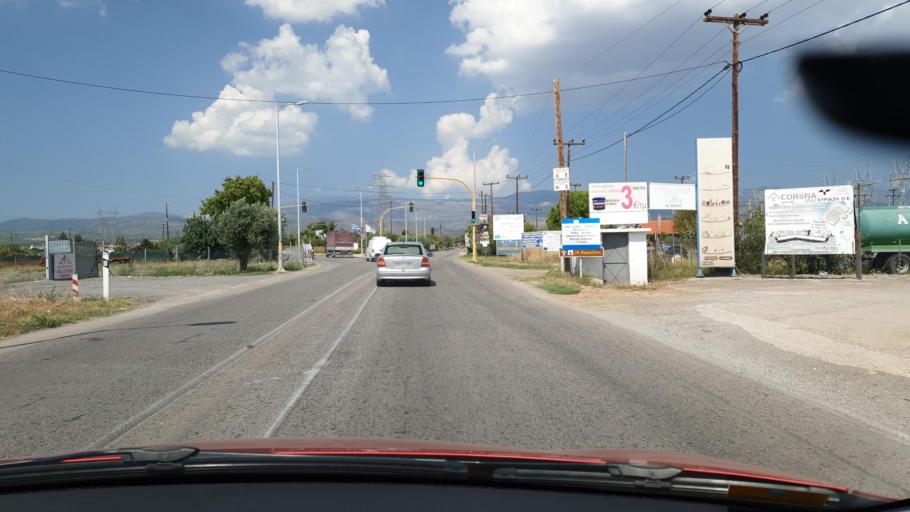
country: GR
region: Central Greece
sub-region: Nomos Evvoias
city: Kastella
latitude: 38.5569
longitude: 23.6327
